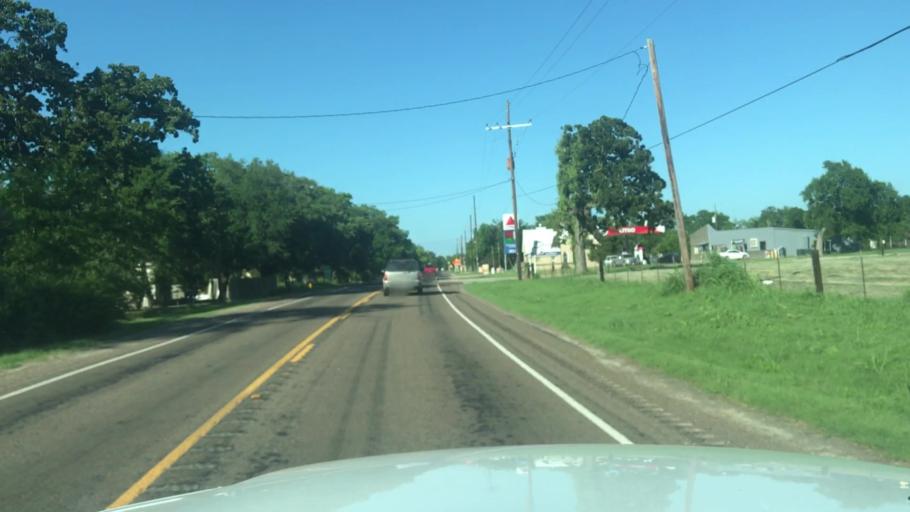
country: US
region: Texas
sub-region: Grimes County
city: Anderson
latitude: 30.6112
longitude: -95.8930
